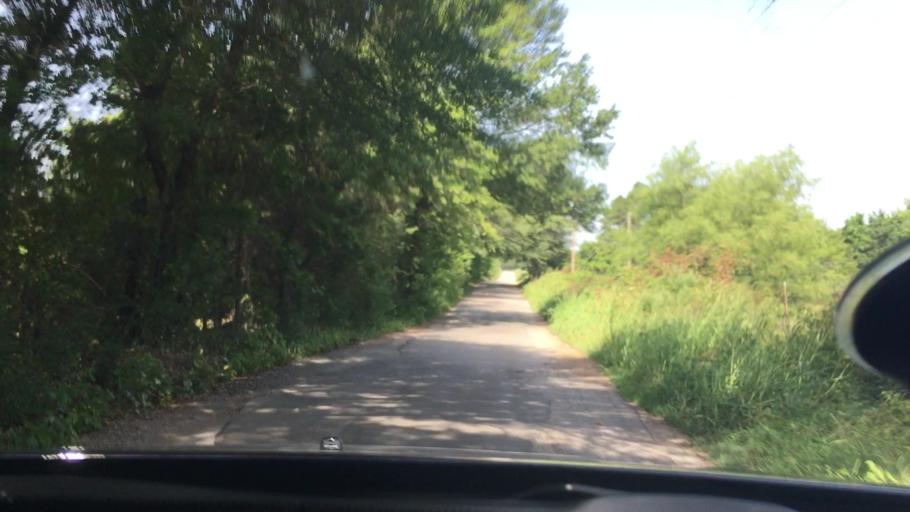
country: US
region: Oklahoma
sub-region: Atoka County
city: Atoka
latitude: 34.3603
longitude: -96.1653
